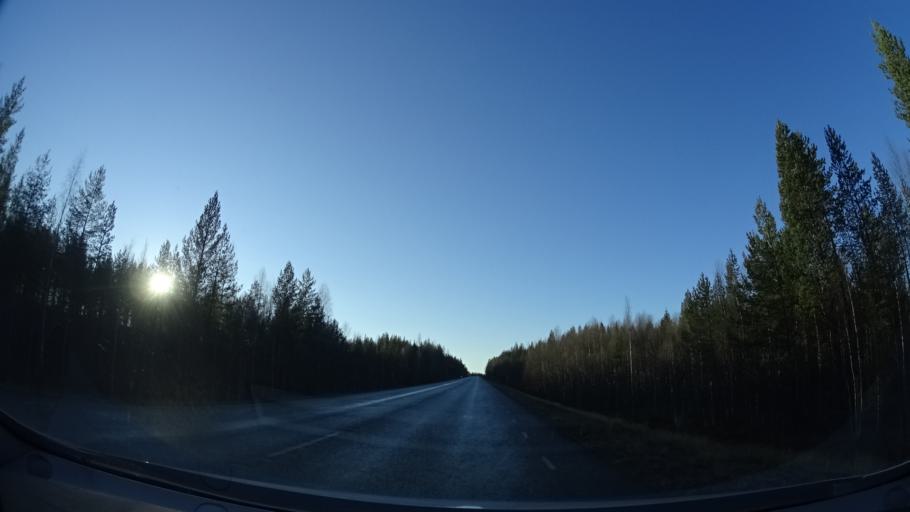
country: SE
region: Vaesterbotten
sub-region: Skelleftea Kommun
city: Boliden
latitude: 64.8772
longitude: 20.3744
